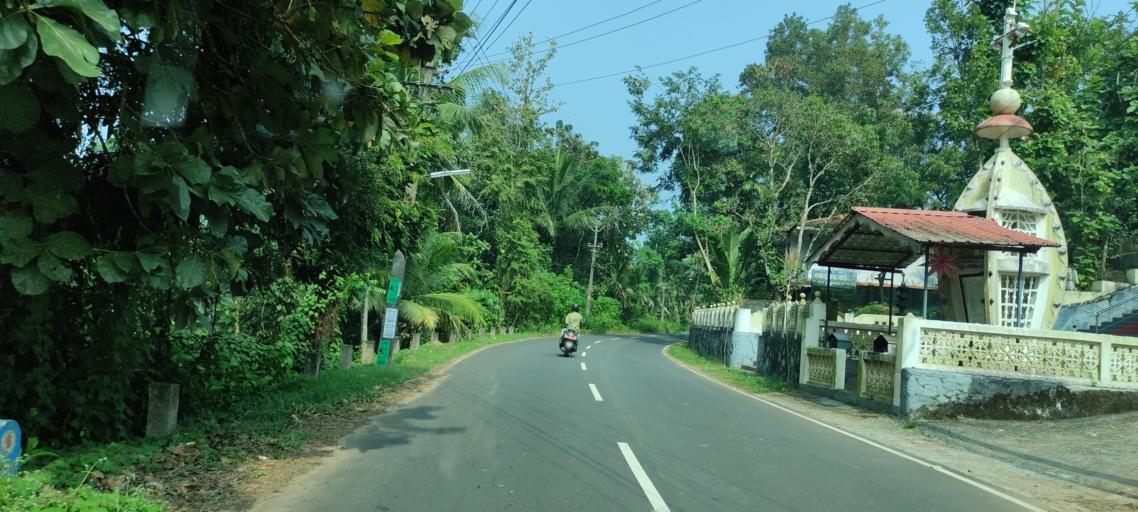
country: IN
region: Kerala
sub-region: Pattanamtitta
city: Adur
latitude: 9.2375
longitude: 76.6923
